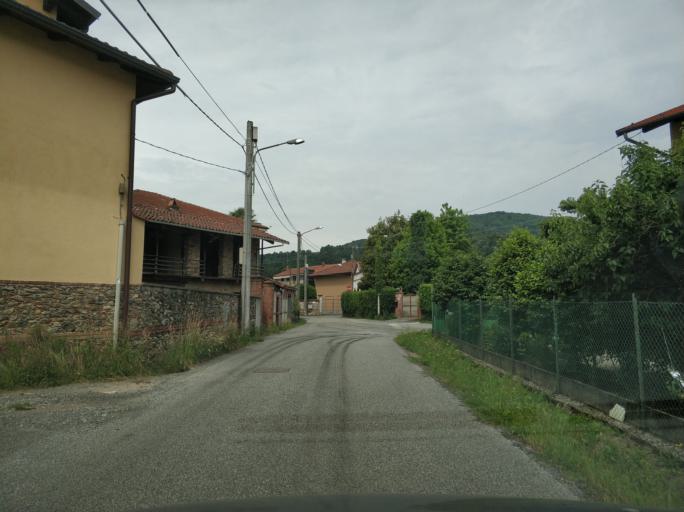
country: IT
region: Piedmont
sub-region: Provincia di Torino
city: Levone
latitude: 45.3171
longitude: 7.6098
